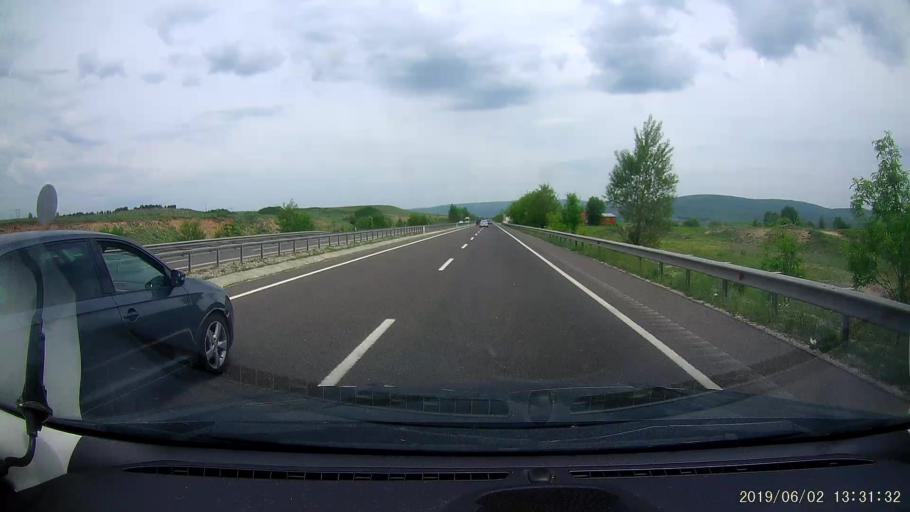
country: TR
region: Cankiri
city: Cerkes
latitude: 40.8061
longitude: 32.9650
